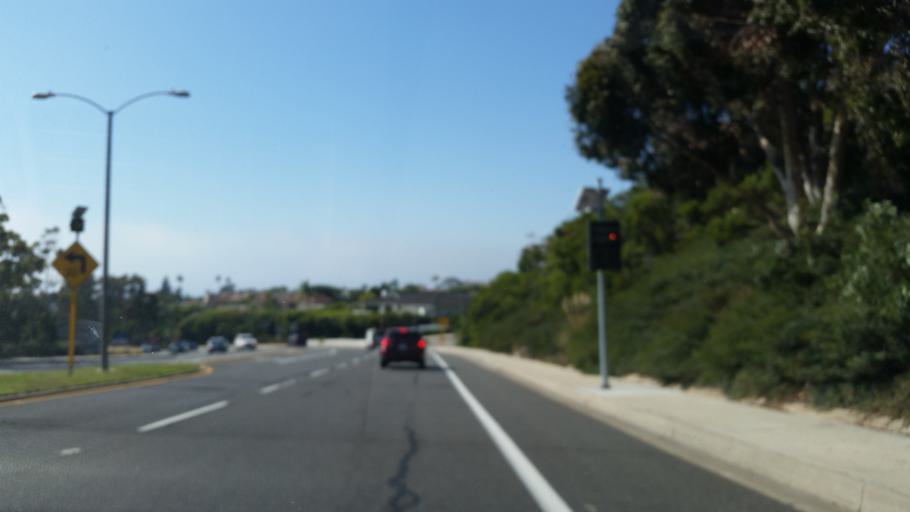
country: US
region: California
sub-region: Orange County
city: Dana Point
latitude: 33.4872
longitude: -117.7250
